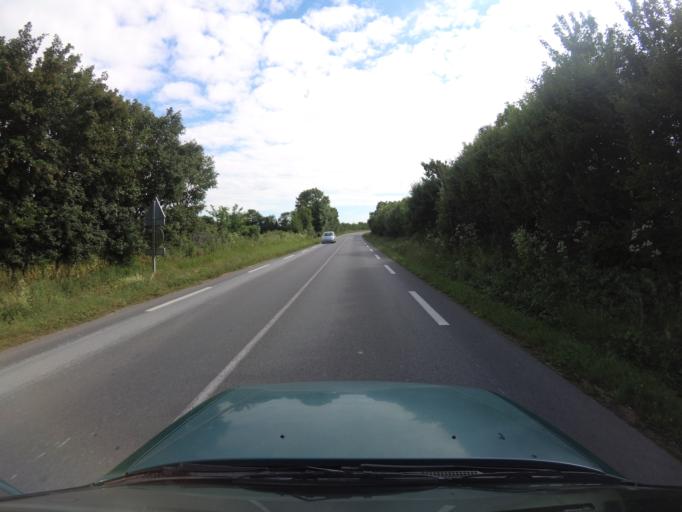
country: FR
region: Poitou-Charentes
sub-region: Departement de la Charente-Maritime
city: Saint-Xandre
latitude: 46.2214
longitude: -1.0859
